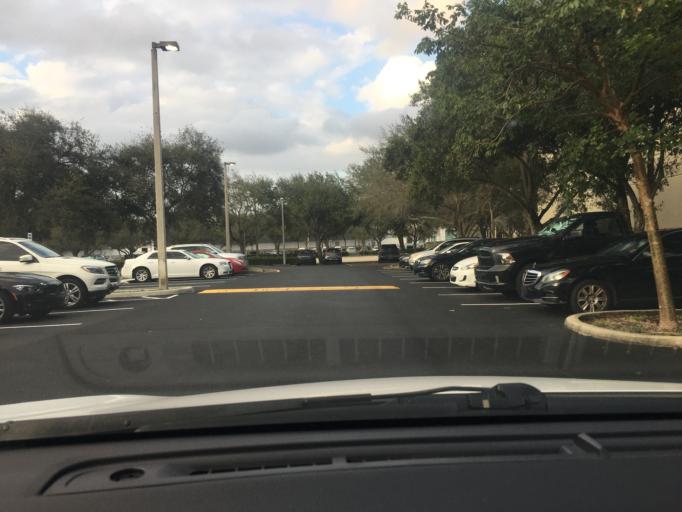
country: US
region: Florida
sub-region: Broward County
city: Dania Beach
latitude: 26.0690
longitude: -80.1809
